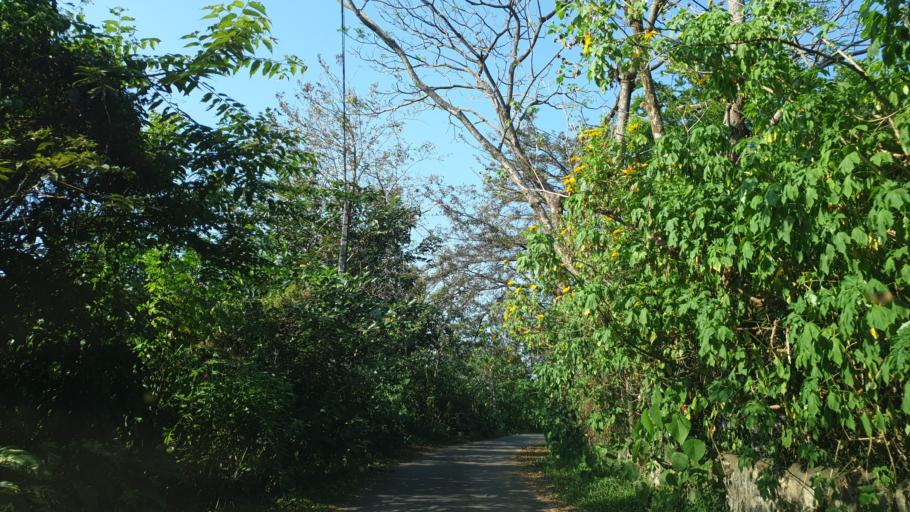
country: LK
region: Western
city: Battaramulla South
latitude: 6.8858
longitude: 79.9480
